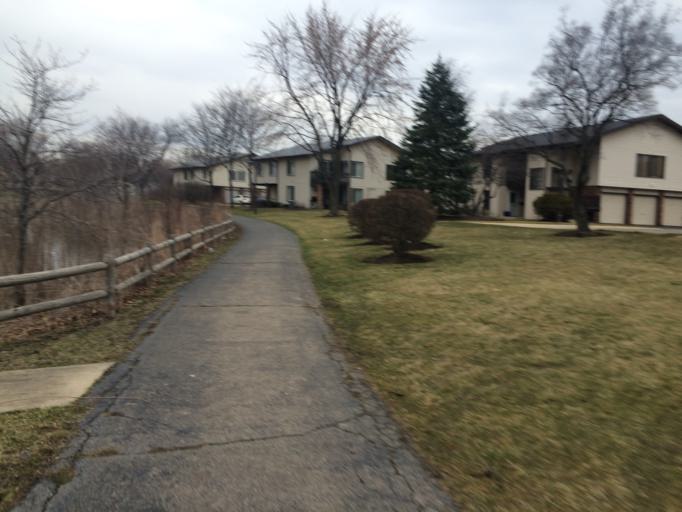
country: US
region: Illinois
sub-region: DuPage County
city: Hanover Park
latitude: 42.0093
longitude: -88.1432
